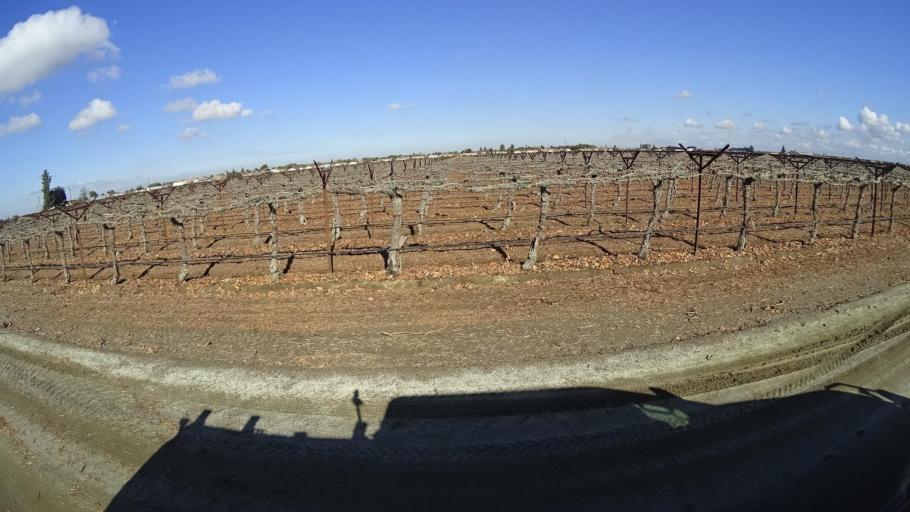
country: US
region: California
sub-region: Kern County
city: McFarland
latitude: 35.6598
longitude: -119.2294
